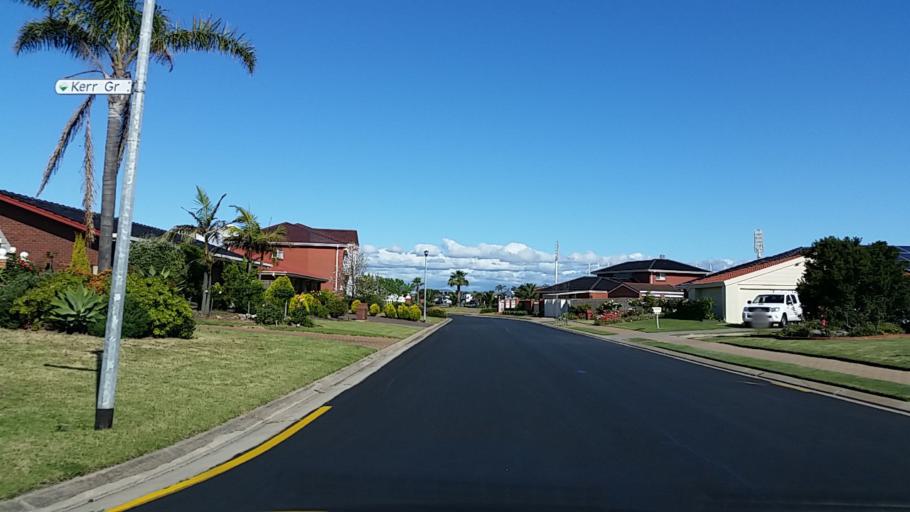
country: AU
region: South Australia
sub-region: Charles Sturt
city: West Lakes Shore
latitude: -34.8744
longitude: 138.4922
